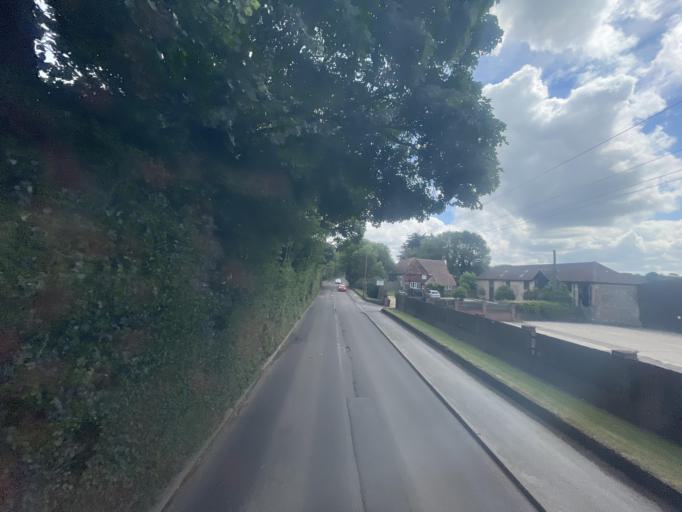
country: GB
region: England
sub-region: Kent
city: Biggin Hill
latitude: 51.2976
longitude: 0.0539
